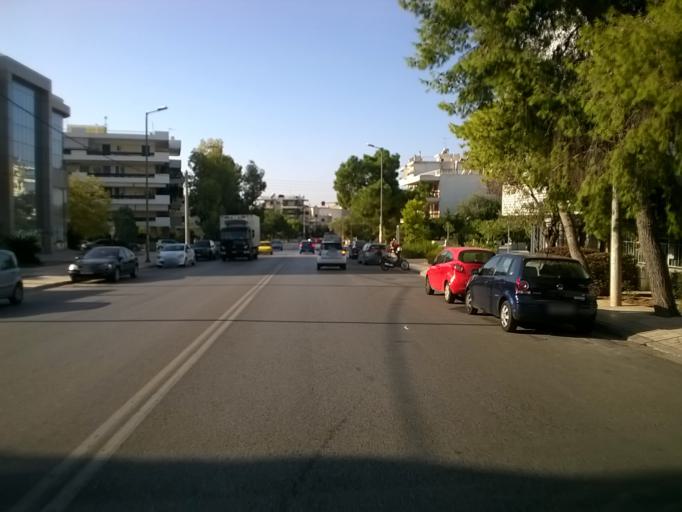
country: GR
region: Attica
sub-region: Nomarchia Athinas
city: Glyfada
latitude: 37.8681
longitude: 23.7577
